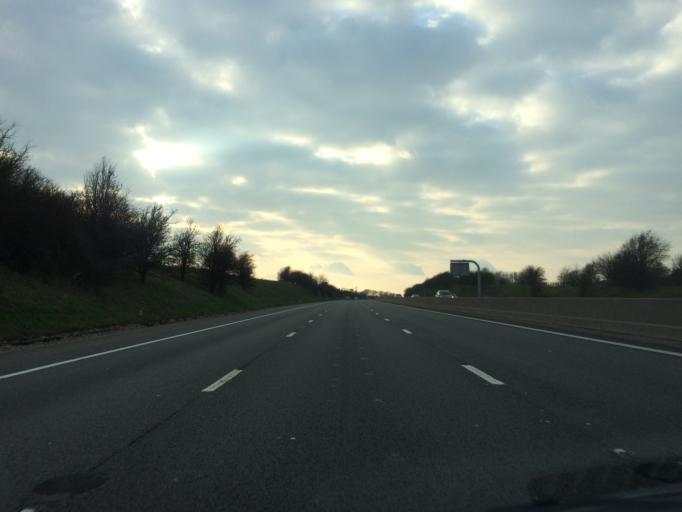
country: GB
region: England
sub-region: Wiltshire
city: Aldbourne
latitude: 51.5069
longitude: -1.6027
